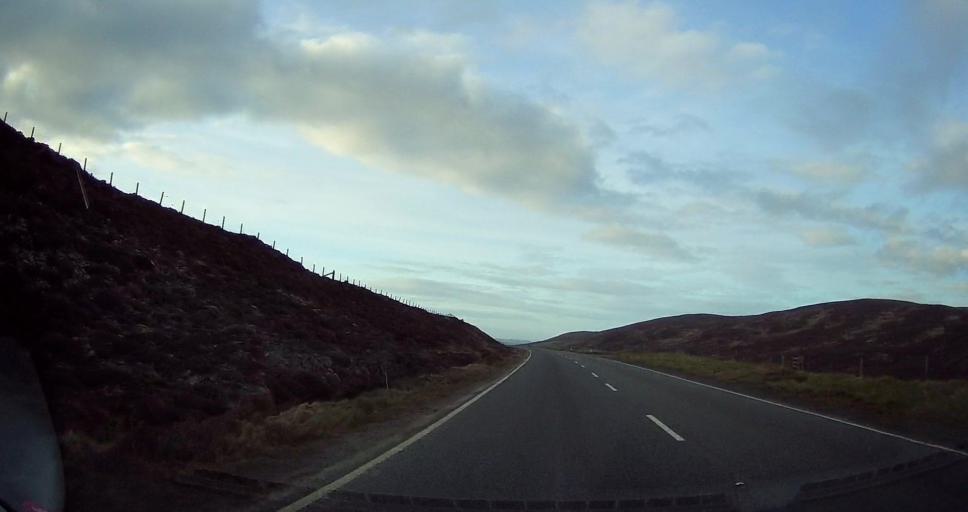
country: GB
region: Scotland
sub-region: Shetland Islands
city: Lerwick
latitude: 60.1449
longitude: -1.2426
